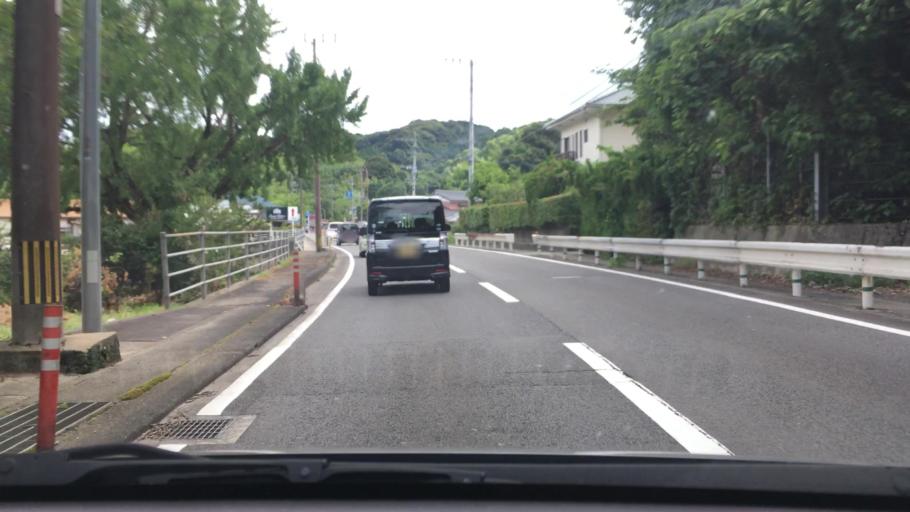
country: JP
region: Nagasaki
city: Togitsu
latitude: 32.9347
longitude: 129.7835
